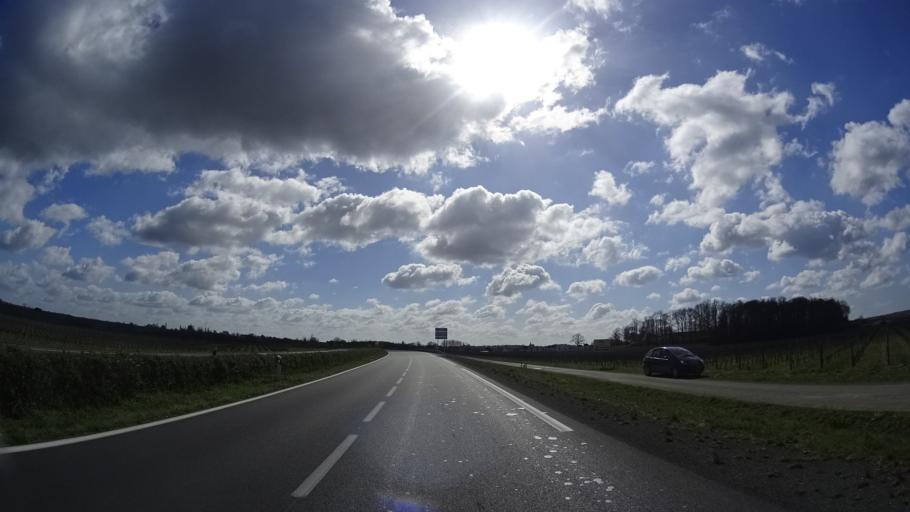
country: FR
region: Pays de la Loire
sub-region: Departement de Maine-et-Loire
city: Brissac-Quince
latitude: 47.3750
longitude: -0.4695
